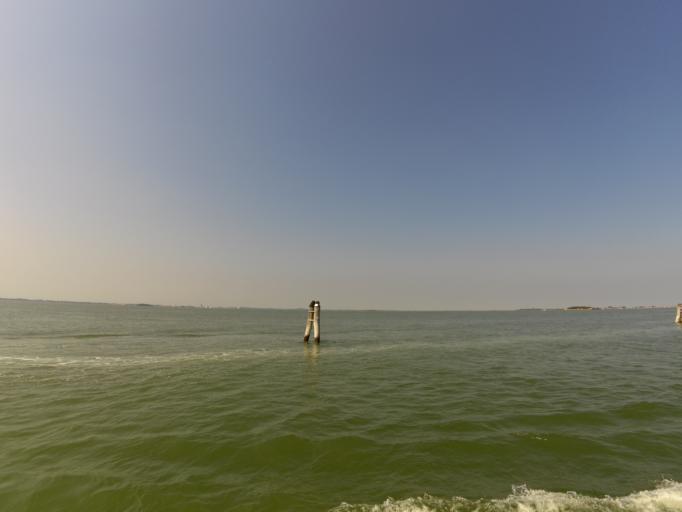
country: IT
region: Veneto
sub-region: Provincia di Venezia
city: Murano
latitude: 45.4593
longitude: 12.3650
